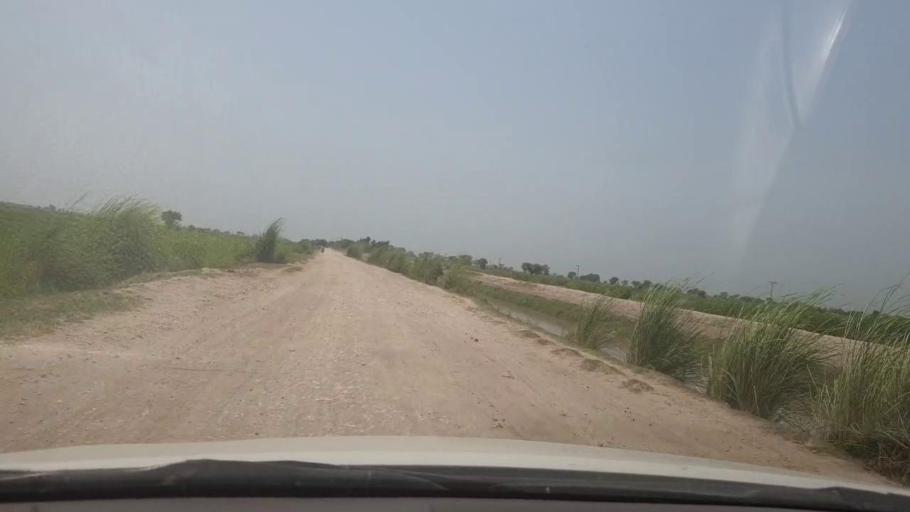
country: PK
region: Sindh
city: Shikarpur
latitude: 28.0516
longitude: 68.5974
